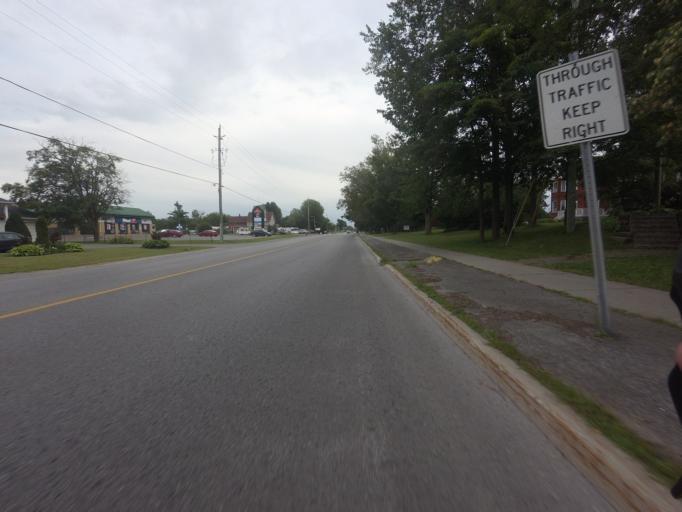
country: CA
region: Ontario
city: Carleton Place
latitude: 45.1307
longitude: -76.1300
